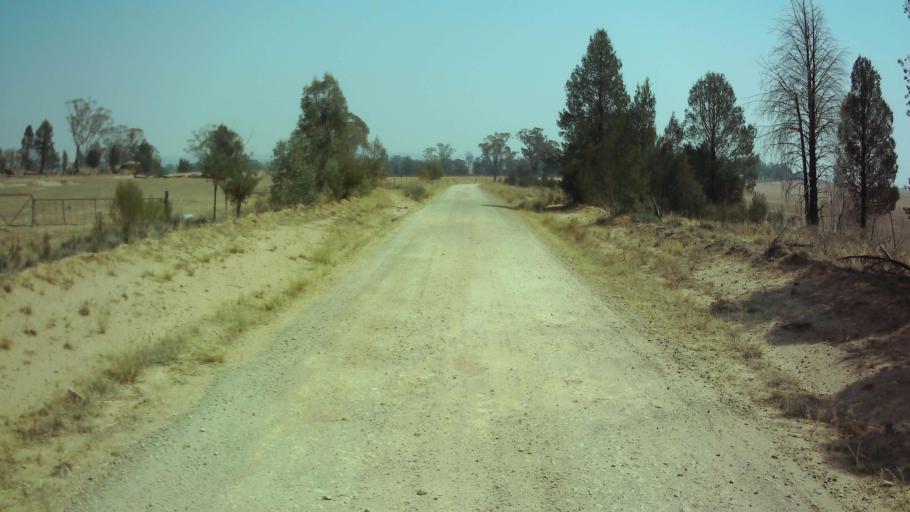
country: AU
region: New South Wales
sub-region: Weddin
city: Grenfell
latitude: -33.6511
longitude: 148.2708
